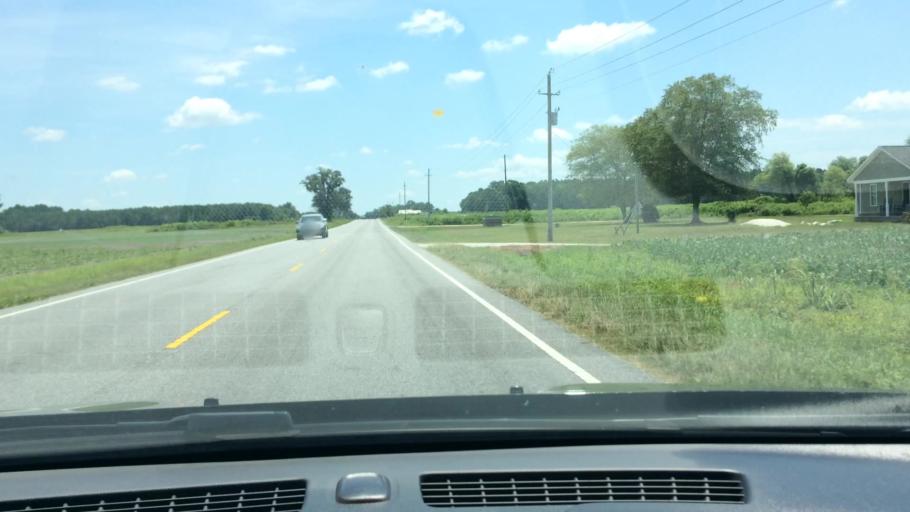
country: US
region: North Carolina
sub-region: Pitt County
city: Ayden
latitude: 35.4715
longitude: -77.3912
